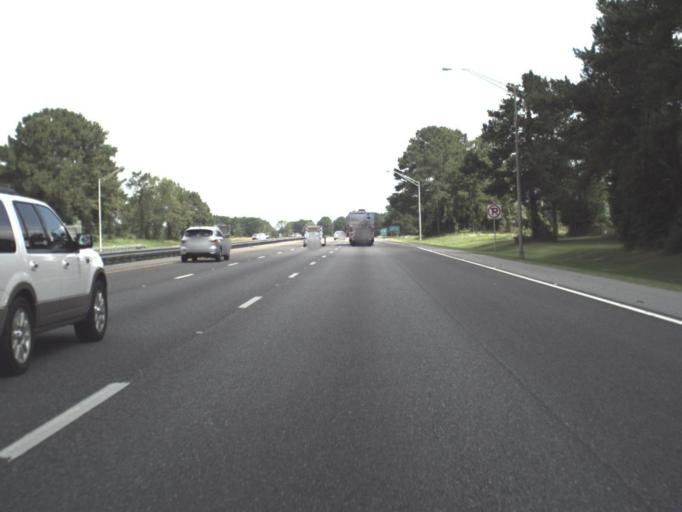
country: US
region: Florida
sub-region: Alachua County
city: High Springs
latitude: 29.9828
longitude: -82.5802
